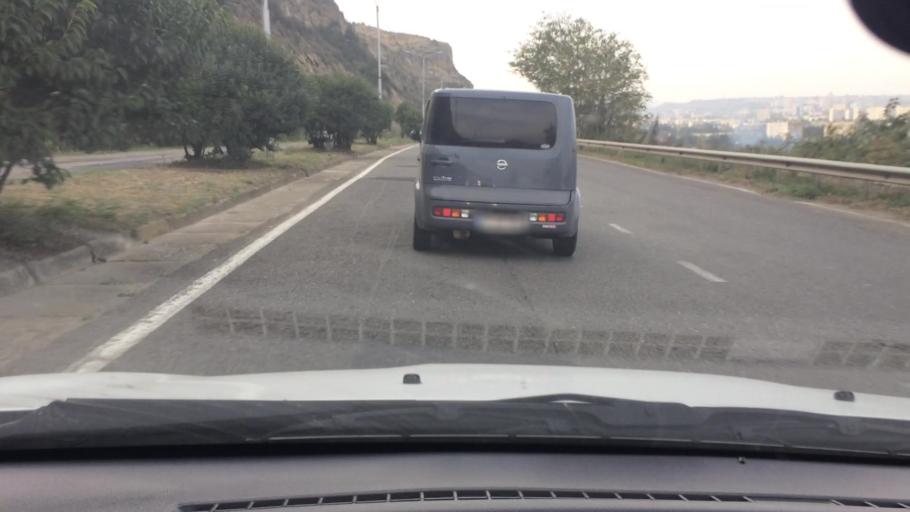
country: GE
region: T'bilisi
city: Tbilisi
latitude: 41.6540
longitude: 44.8997
